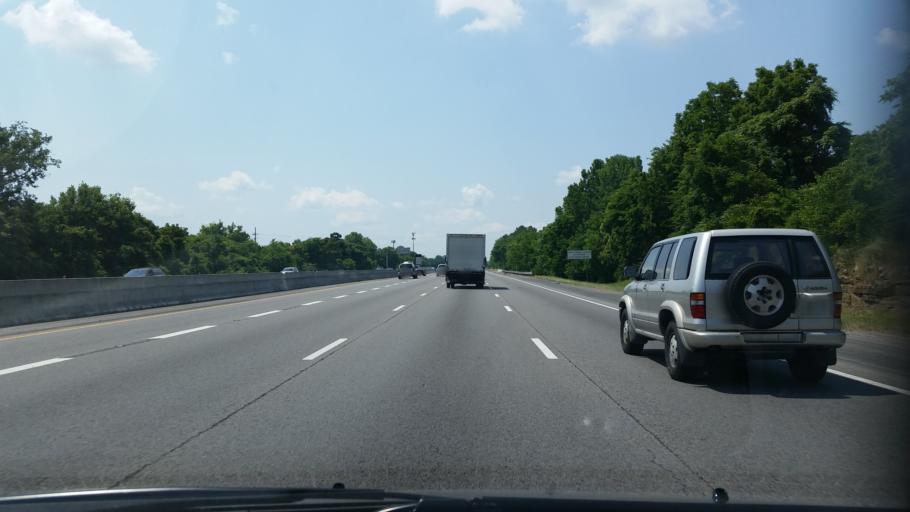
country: US
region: Tennessee
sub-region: Davidson County
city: Oak Hill
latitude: 36.0683
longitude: -86.7706
